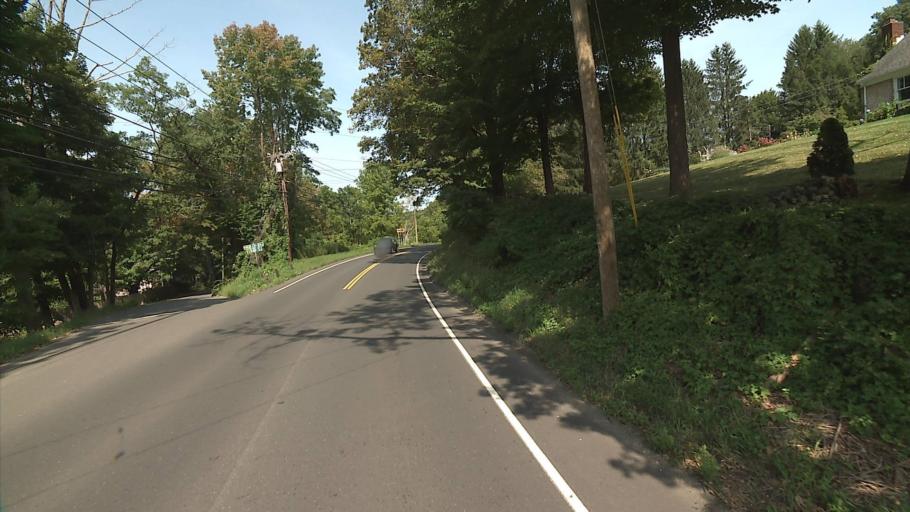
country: US
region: Connecticut
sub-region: Fairfield County
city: Newtown
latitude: 41.3909
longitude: -73.3291
